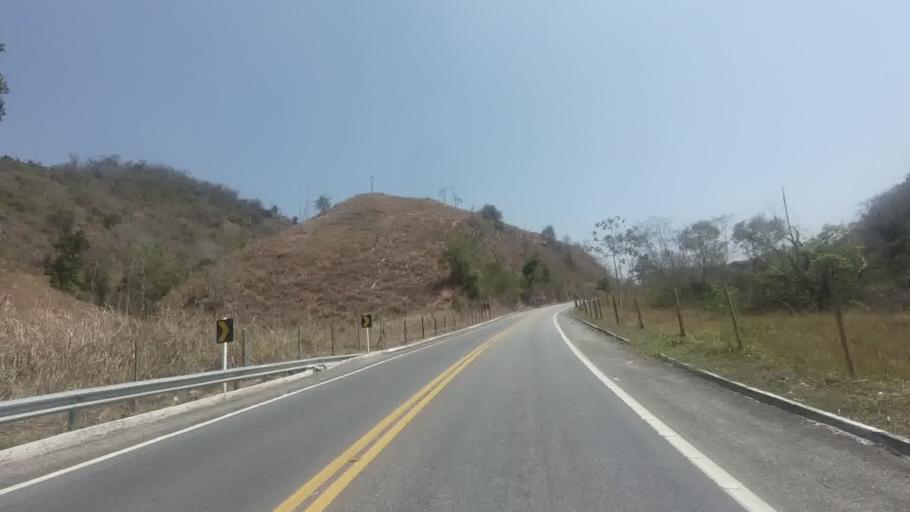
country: BR
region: Espirito Santo
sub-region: Cachoeiro De Itapemirim
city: Cachoeiro de Itapemirim
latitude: -20.8294
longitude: -41.2191
